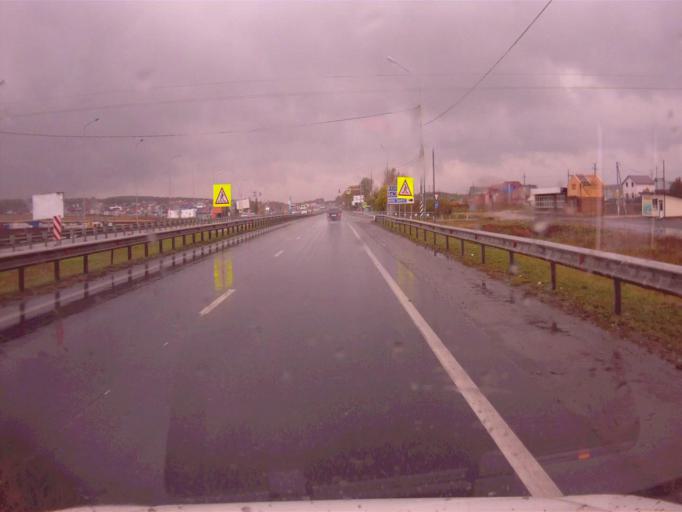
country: RU
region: Chelyabinsk
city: Dolgoderevenskoye
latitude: 55.2726
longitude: 61.3443
